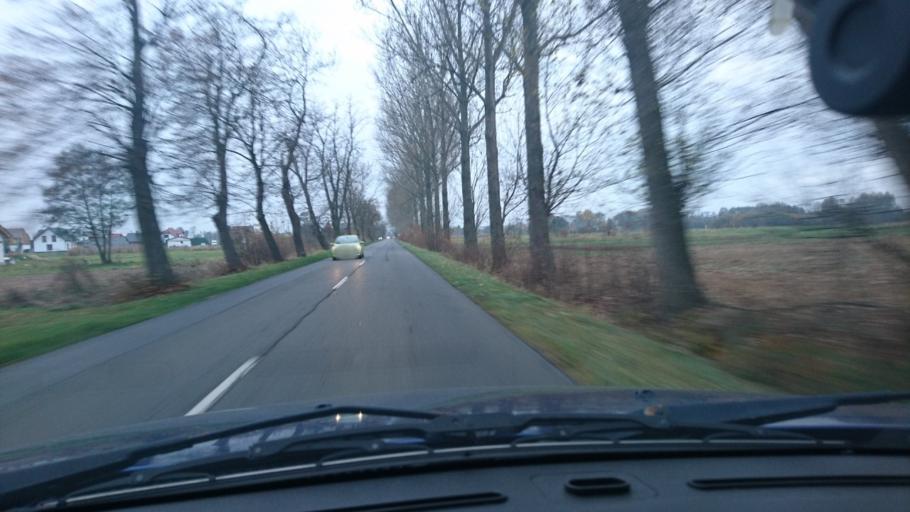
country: PL
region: Greater Poland Voivodeship
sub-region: Powiat ostrowski
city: Odolanow
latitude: 51.5480
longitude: 17.6574
